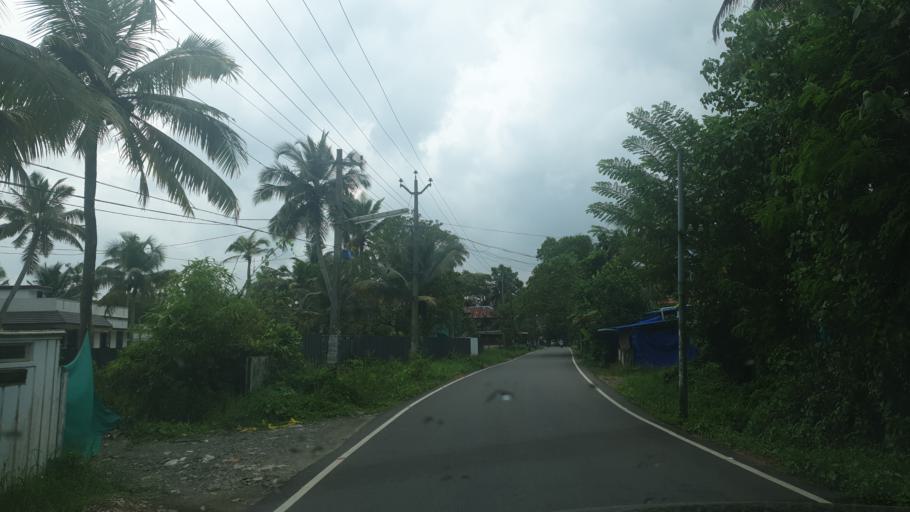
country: IN
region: Kerala
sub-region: Ernakulam
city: Cochin
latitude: 10.0027
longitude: 76.2281
